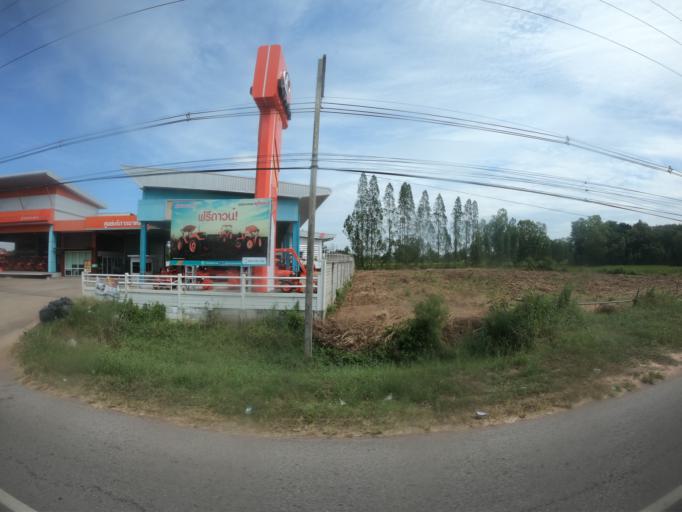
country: TH
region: Maha Sarakham
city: Chiang Yuen
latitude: 16.4227
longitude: 103.0724
